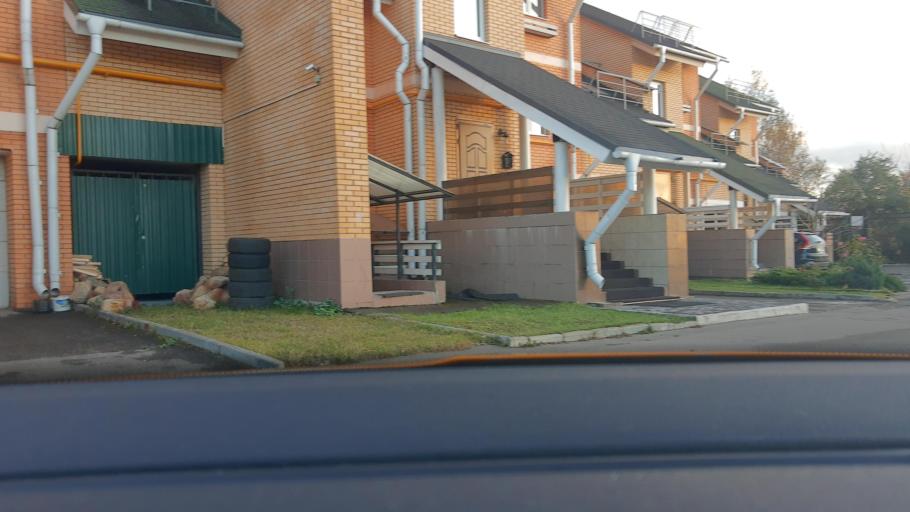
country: RU
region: Moscow
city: Rublevo
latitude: 55.7844
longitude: 37.3935
